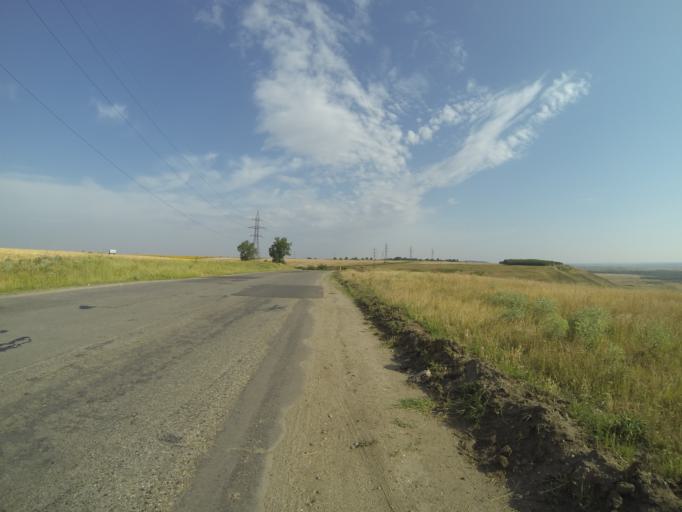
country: RO
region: Dolj
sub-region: Comuna Dranicu
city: Padea
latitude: 44.0067
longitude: 23.8741
